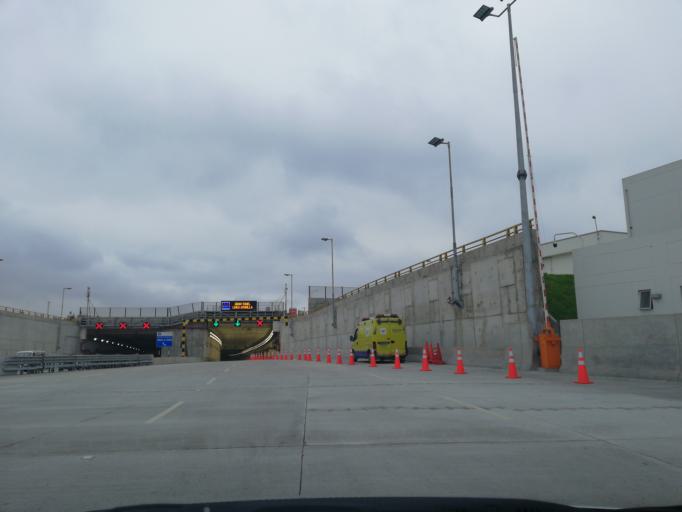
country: PE
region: Lima
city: Lima
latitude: -12.0433
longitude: -77.0206
